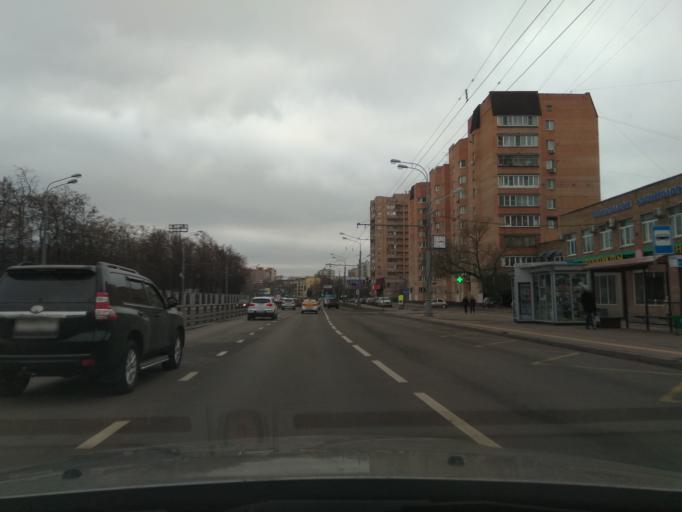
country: RU
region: Moskovskaya
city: Koptevo
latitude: 55.8331
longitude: 37.5329
